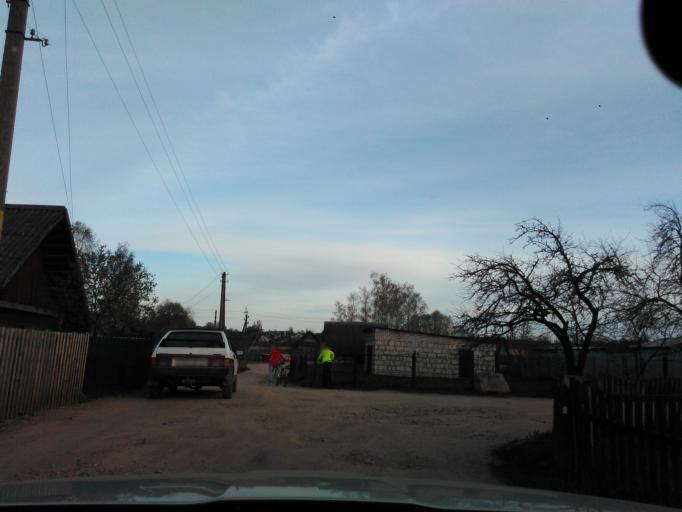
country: BY
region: Vitebsk
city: Chashniki
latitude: 54.8591
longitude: 29.1683
